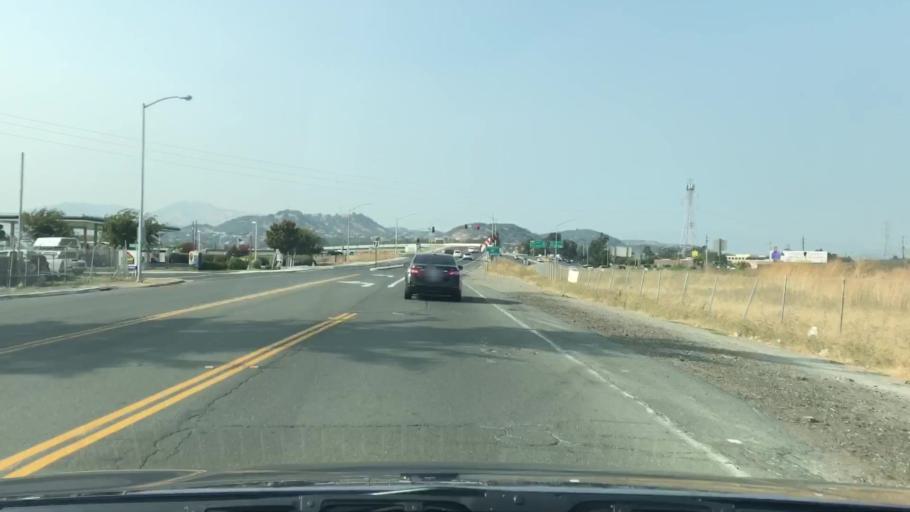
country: US
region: California
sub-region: Solano County
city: Green Valley
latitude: 38.2121
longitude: -122.1385
